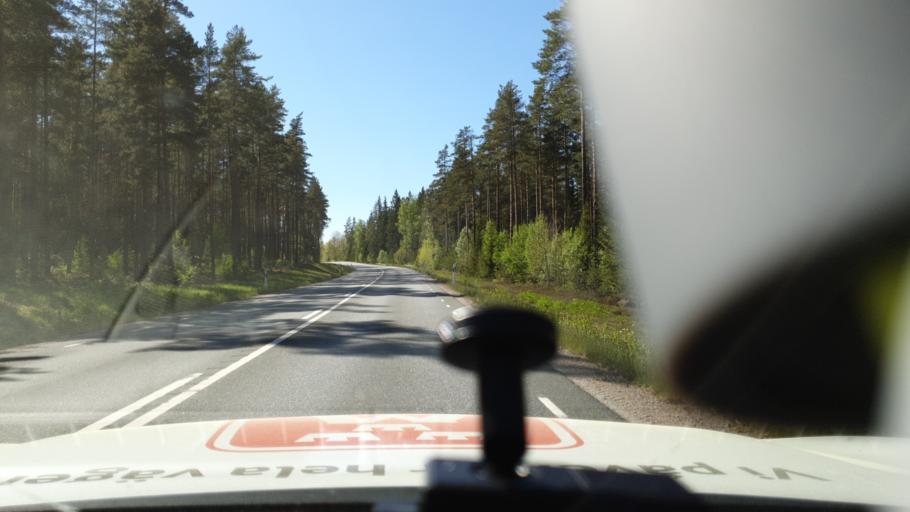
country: SE
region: Kronoberg
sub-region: Uppvidinge Kommun
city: Aseda
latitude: 57.3999
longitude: 15.3364
